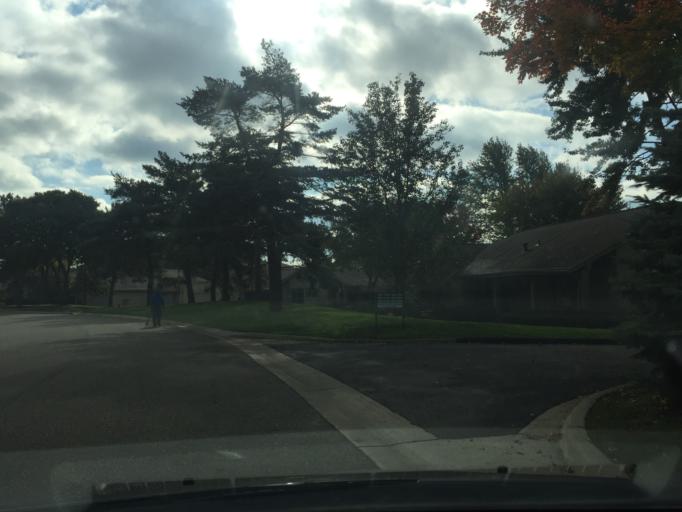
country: US
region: Michigan
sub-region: Oakland County
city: Sylvan Lake
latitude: 42.5814
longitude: -83.3185
